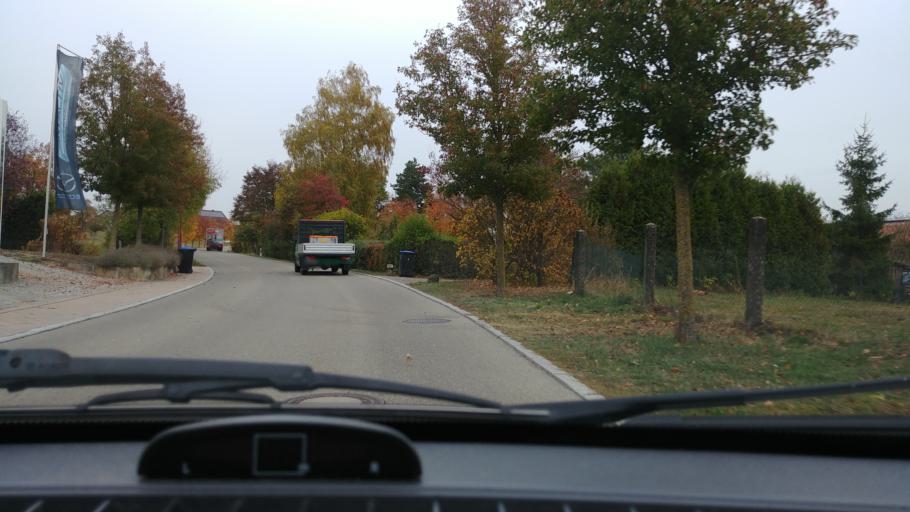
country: DE
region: Baden-Wuerttemberg
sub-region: Regierungsbezirk Stuttgart
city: Rot am See
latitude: 49.2676
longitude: 10.0706
